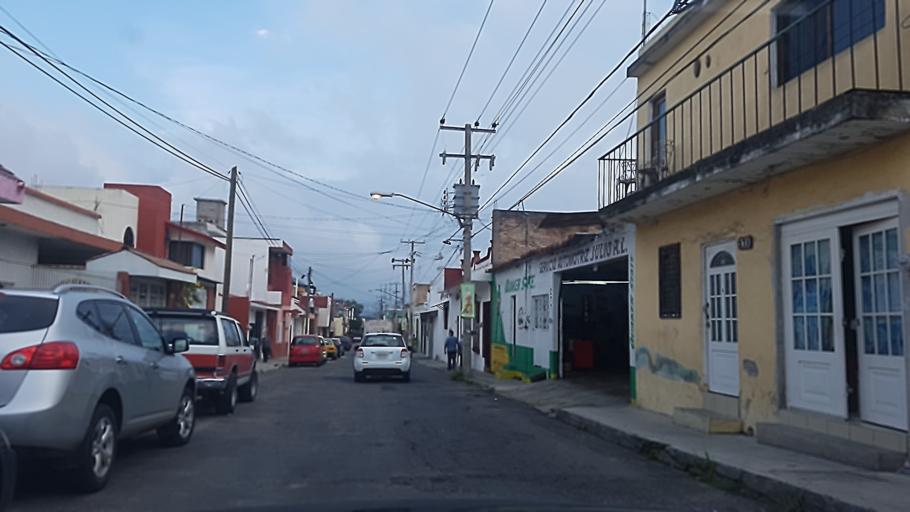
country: MX
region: Nayarit
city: Tepic
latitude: 21.5078
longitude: -104.8990
